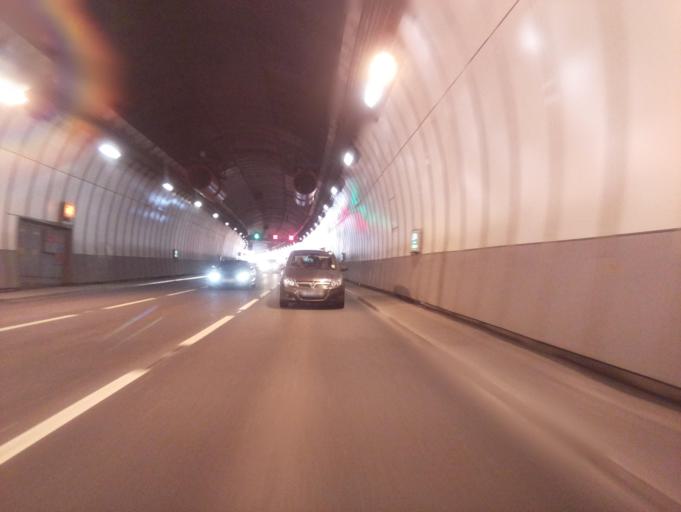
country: GB
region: England
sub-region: Cornwall
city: Saltash
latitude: 50.4117
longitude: -4.2156
